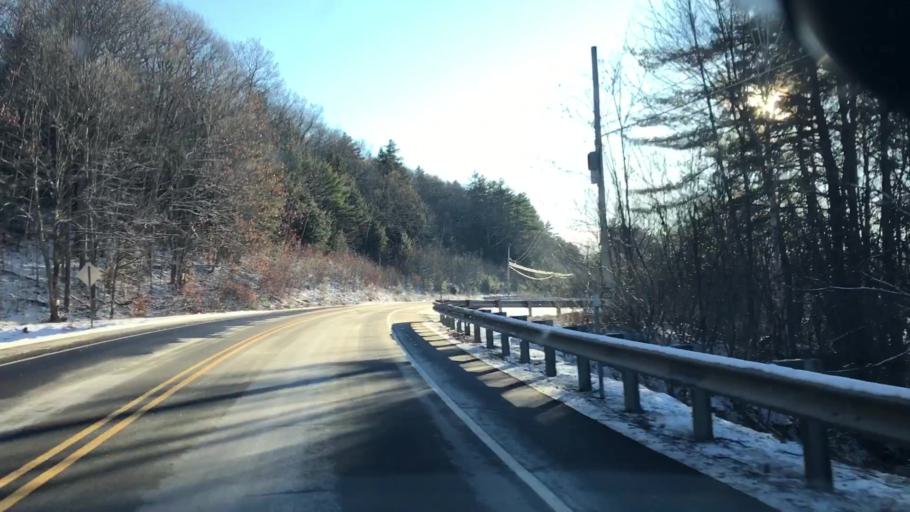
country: US
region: New Hampshire
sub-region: Grafton County
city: Orford
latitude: 43.9544
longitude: -72.0986
